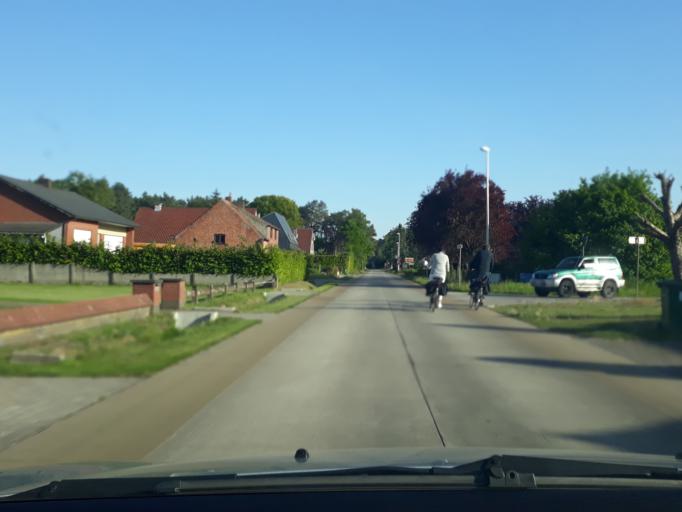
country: BE
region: Flanders
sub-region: Provincie Antwerpen
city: Vorselaar
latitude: 51.2171
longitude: 4.7552
